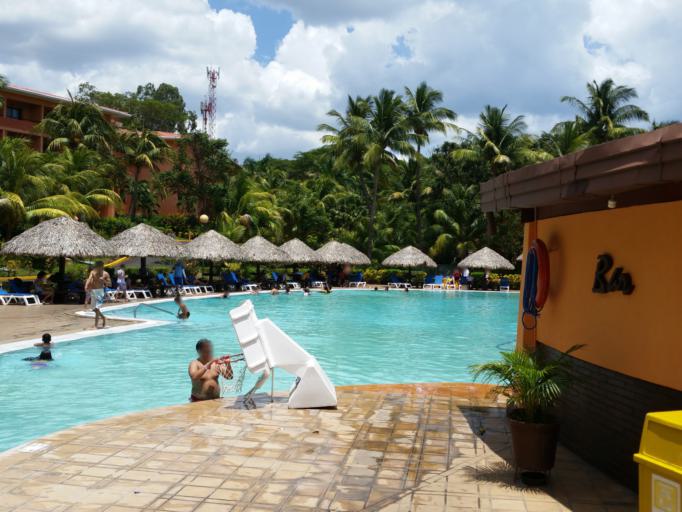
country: NI
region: Managua
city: Masachapa
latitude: 11.8080
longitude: -86.5197
